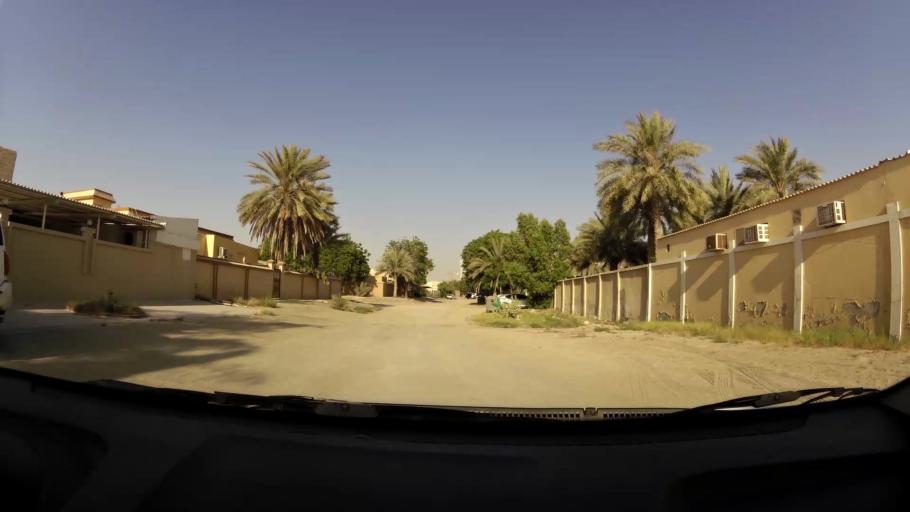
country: AE
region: Ajman
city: Ajman
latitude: 25.3999
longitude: 55.4680
